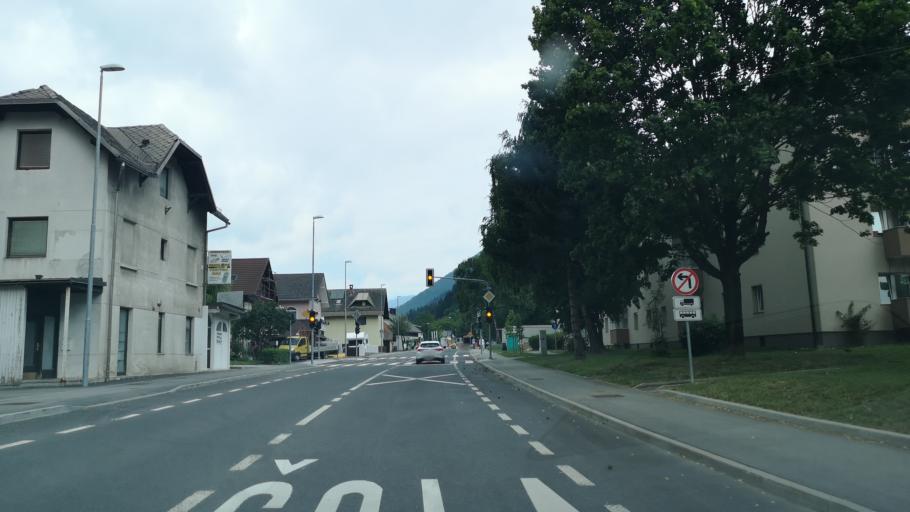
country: SI
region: Jesenice
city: Hrusica
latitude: 46.4407
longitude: 14.0407
